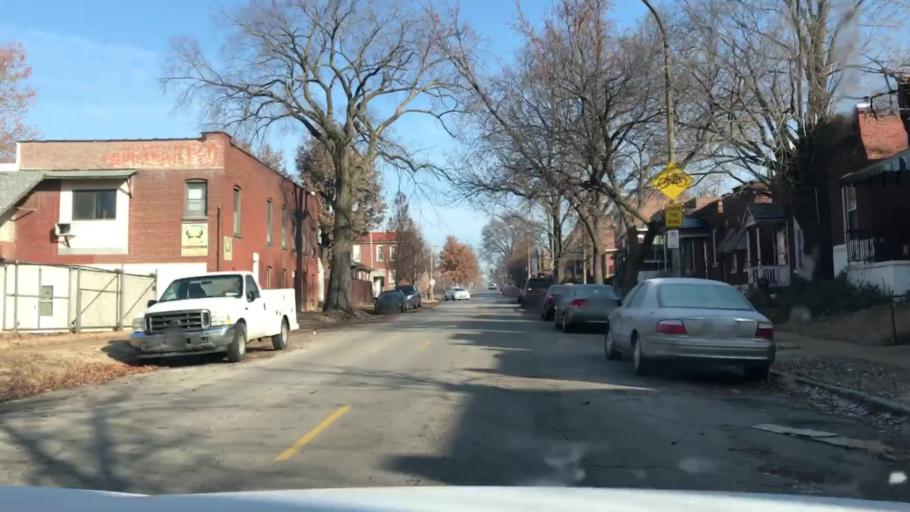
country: US
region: Missouri
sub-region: City of Saint Louis
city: St. Louis
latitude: 38.5957
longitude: -90.2367
